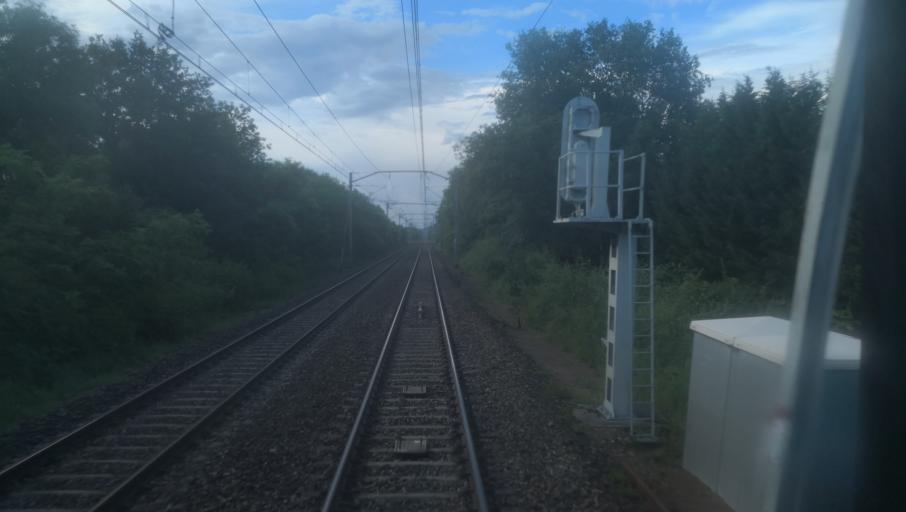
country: FR
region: Centre
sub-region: Departement du Loir-et-Cher
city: Nouan-le-Fuzelier
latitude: 47.5414
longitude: 2.0322
